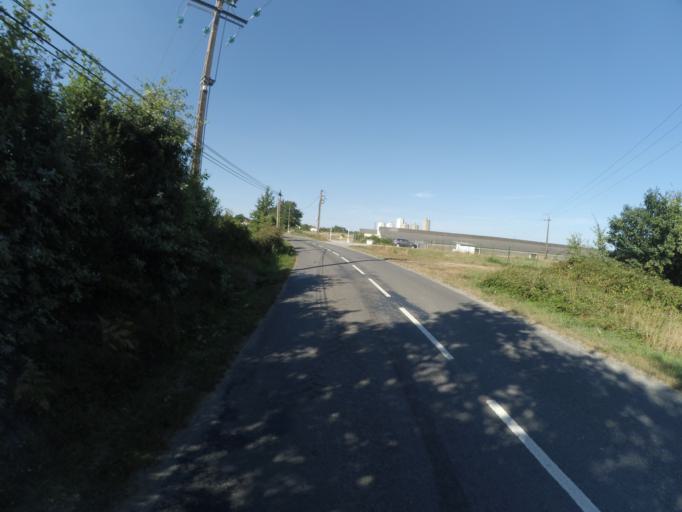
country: FR
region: Pays de la Loire
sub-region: Departement de la Loire-Atlantique
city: La Planche
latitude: 47.0196
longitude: -1.4120
